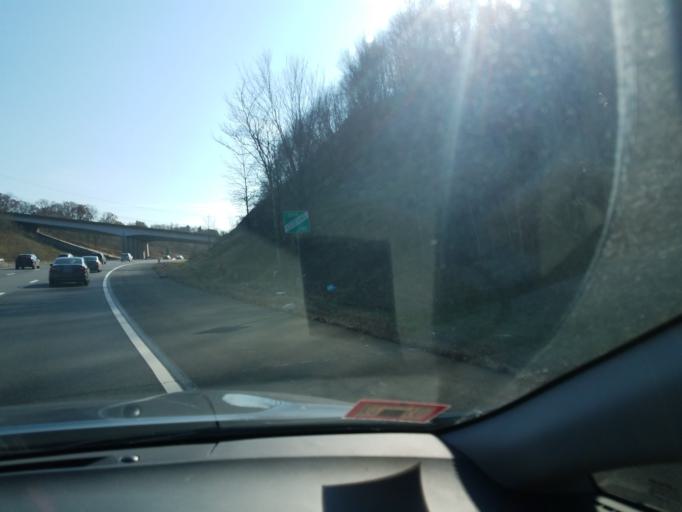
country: US
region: Pennsylvania
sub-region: Allegheny County
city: West View
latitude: 40.5188
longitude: -80.0550
